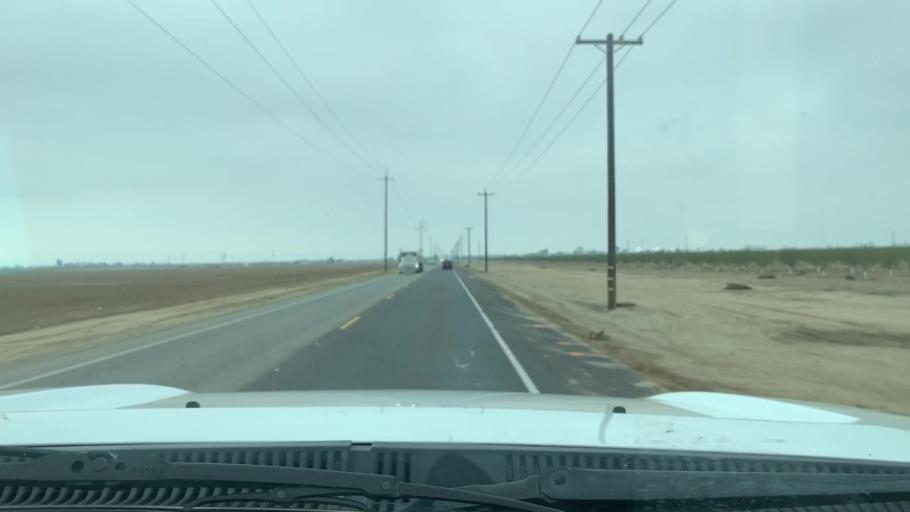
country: US
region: California
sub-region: Kern County
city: Shafter
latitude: 35.4417
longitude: -119.2301
